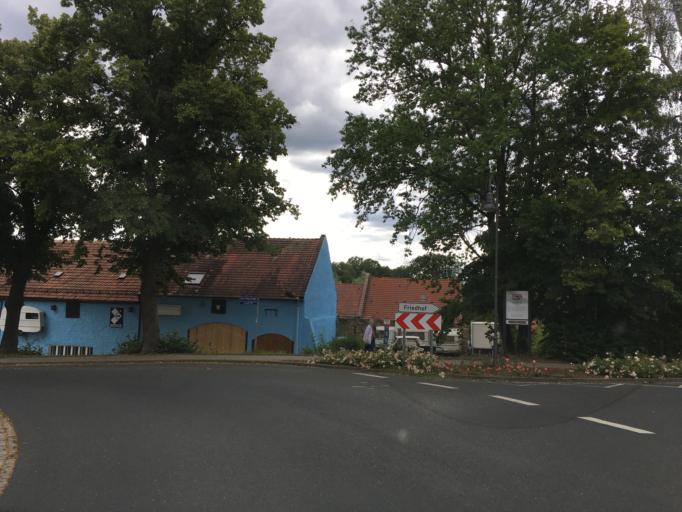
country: DE
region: Saxony
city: Radeberg
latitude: 51.1200
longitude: 13.9178
